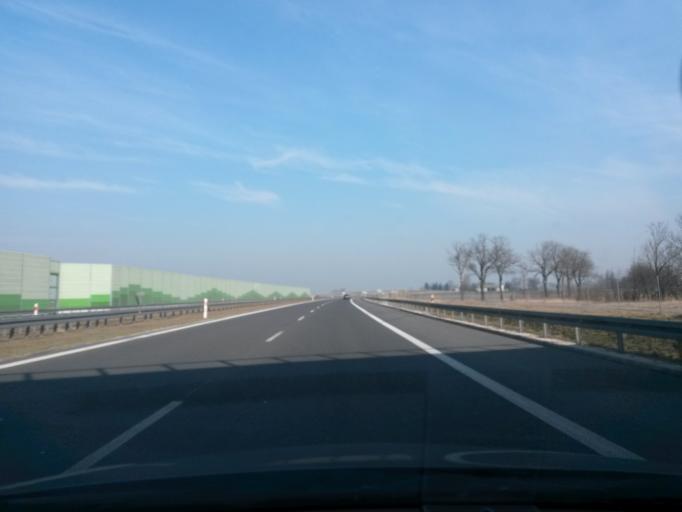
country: PL
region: Lodz Voivodeship
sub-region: Powiat kutnowski
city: Krzyzanow
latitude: 52.1477
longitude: 19.4818
